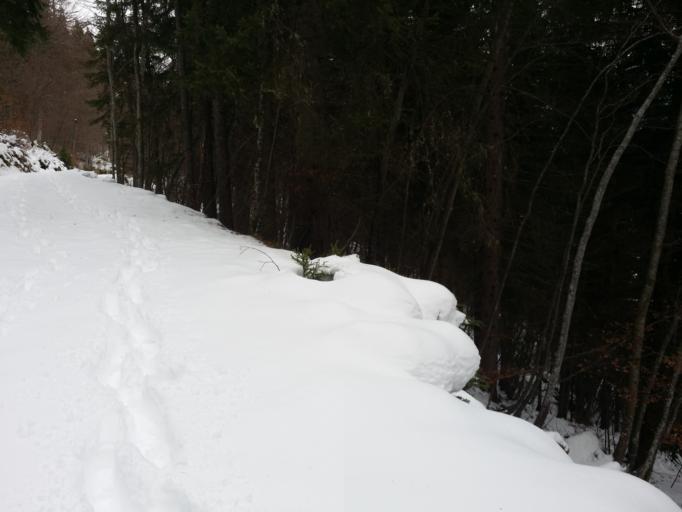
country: IT
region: Piedmont
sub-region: Provincia Verbano-Cusio-Ossola
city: Crodo
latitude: 46.2185
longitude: 8.2918
